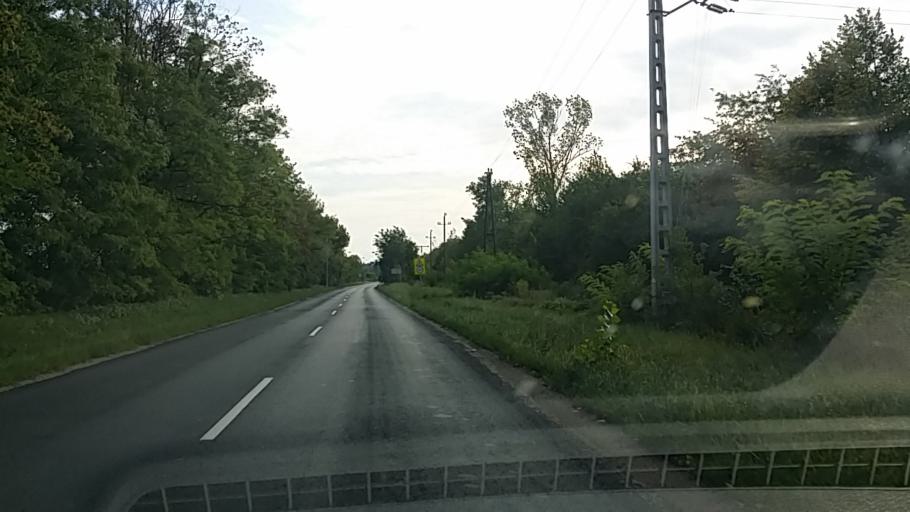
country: HU
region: Gyor-Moson-Sopron
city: Fertorakos
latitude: 47.7173
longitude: 16.6156
